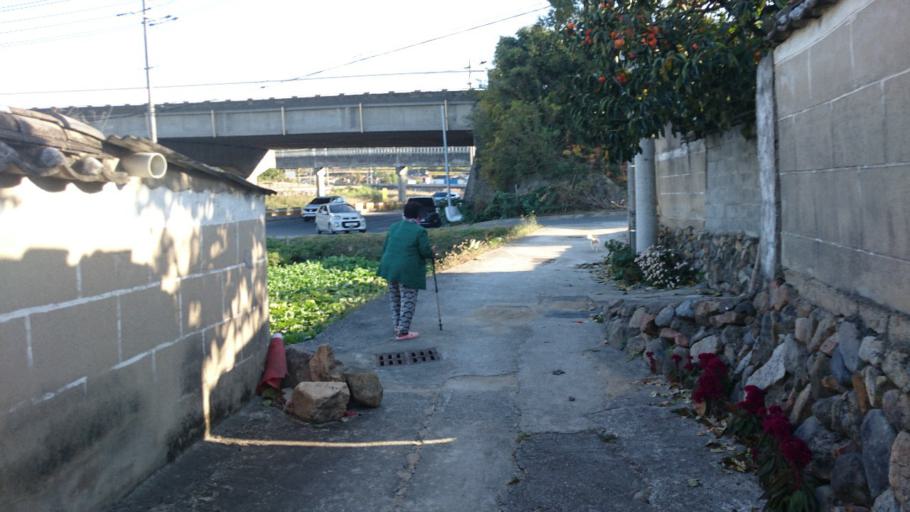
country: KR
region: Gyeongsangbuk-do
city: Kyonju
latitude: 35.8261
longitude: 129.2255
